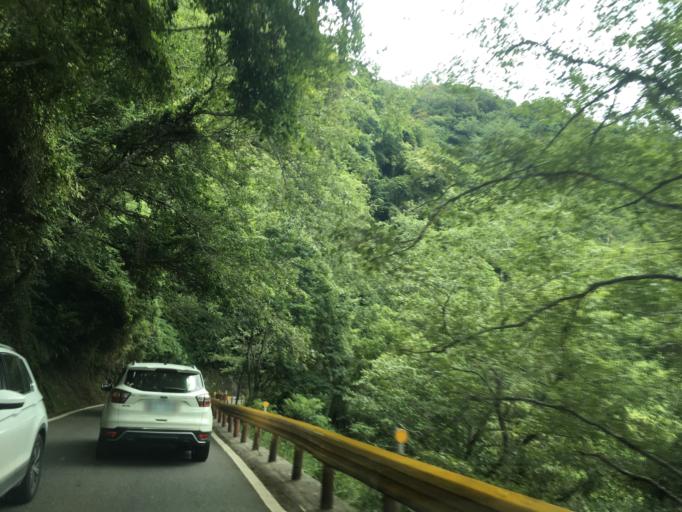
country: TW
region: Taiwan
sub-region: Hualien
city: Hualian
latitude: 24.1881
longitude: 121.4106
